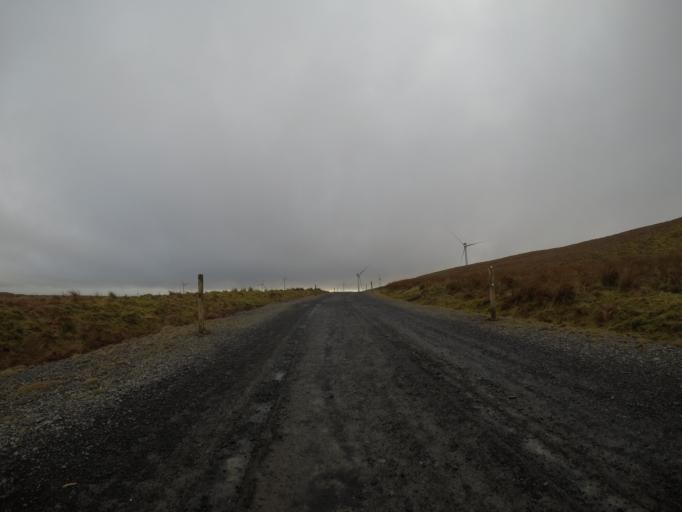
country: GB
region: Scotland
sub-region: North Ayrshire
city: Fairlie
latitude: 55.7610
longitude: -4.7916
